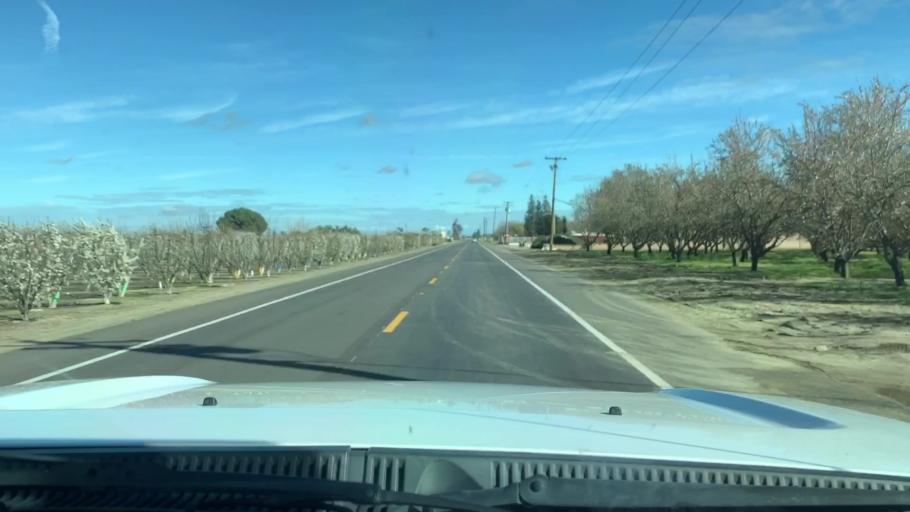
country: US
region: California
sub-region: Fresno County
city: Laton
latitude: 36.4994
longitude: -119.6830
